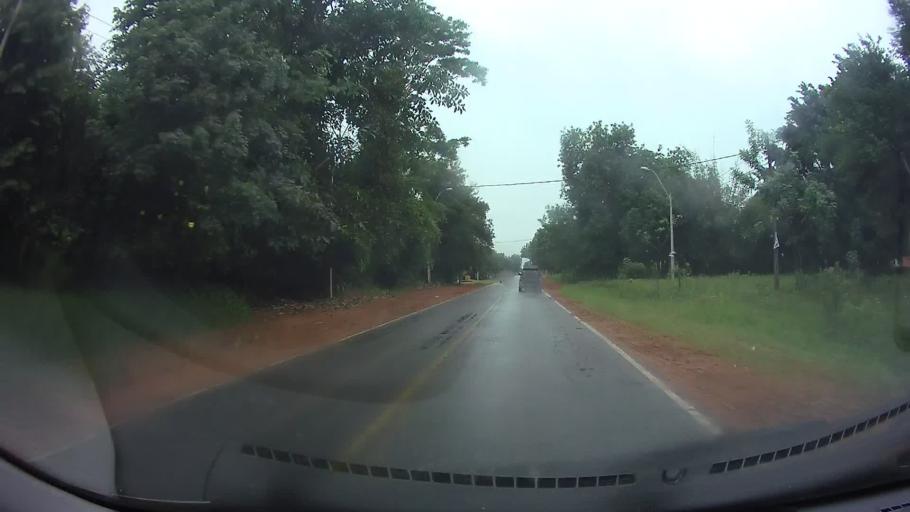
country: PY
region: Central
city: Ita
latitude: -25.4924
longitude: -57.3591
